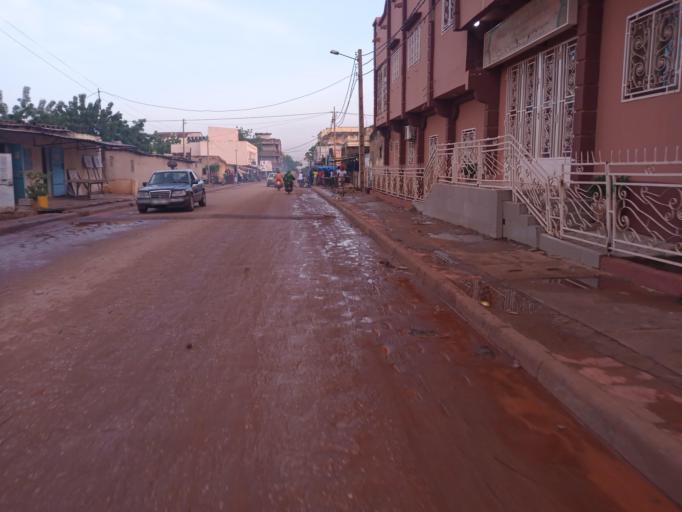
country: ML
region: Bamako
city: Bamako
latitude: 12.6414
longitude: -8.0306
